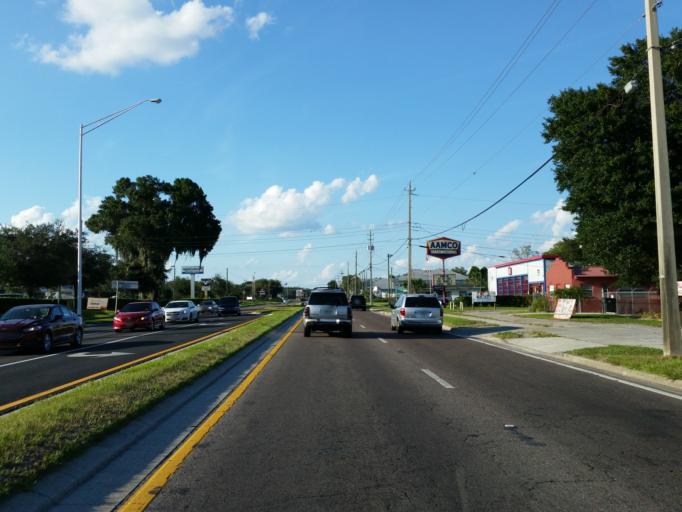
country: US
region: Florida
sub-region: Hillsborough County
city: Plant City
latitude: 27.9819
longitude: -82.1215
